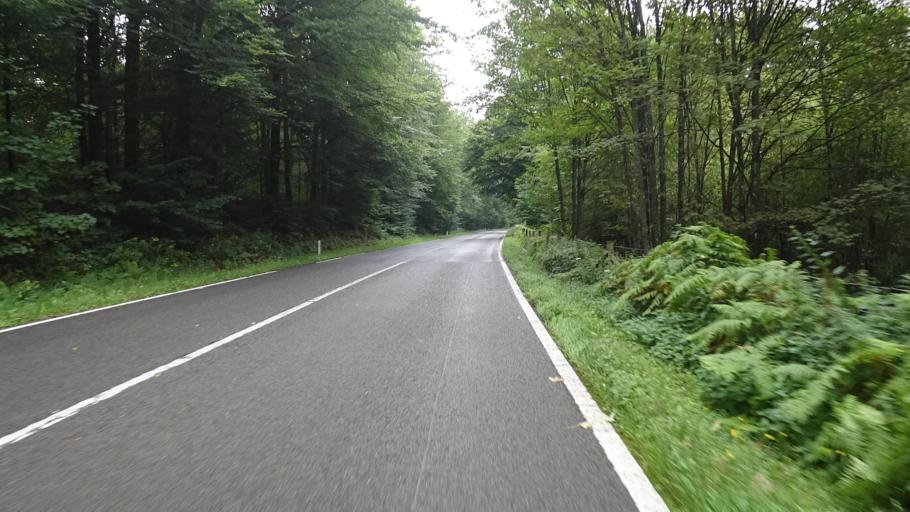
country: BE
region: Wallonia
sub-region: Province du Luxembourg
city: Chiny
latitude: 49.7845
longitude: 5.3307
